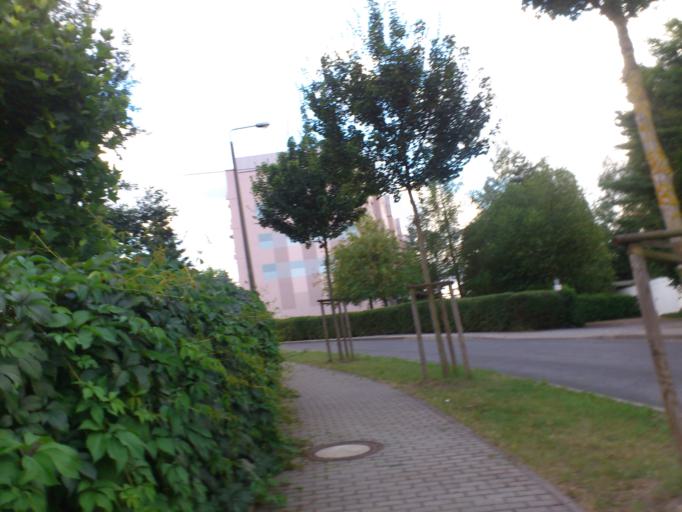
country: DE
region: Saxony
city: Dresden
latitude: 51.0203
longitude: 13.7738
